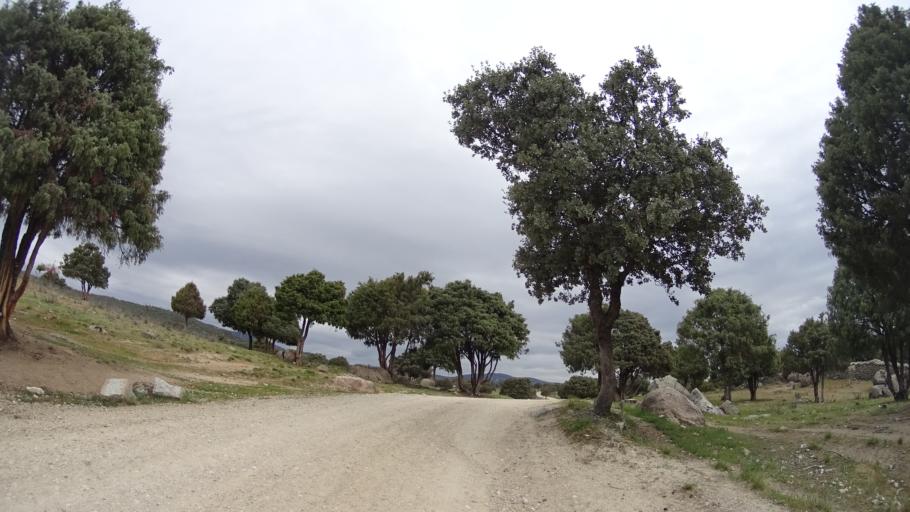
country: ES
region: Madrid
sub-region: Provincia de Madrid
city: Hoyo de Manzanares
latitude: 40.6038
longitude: -3.8784
